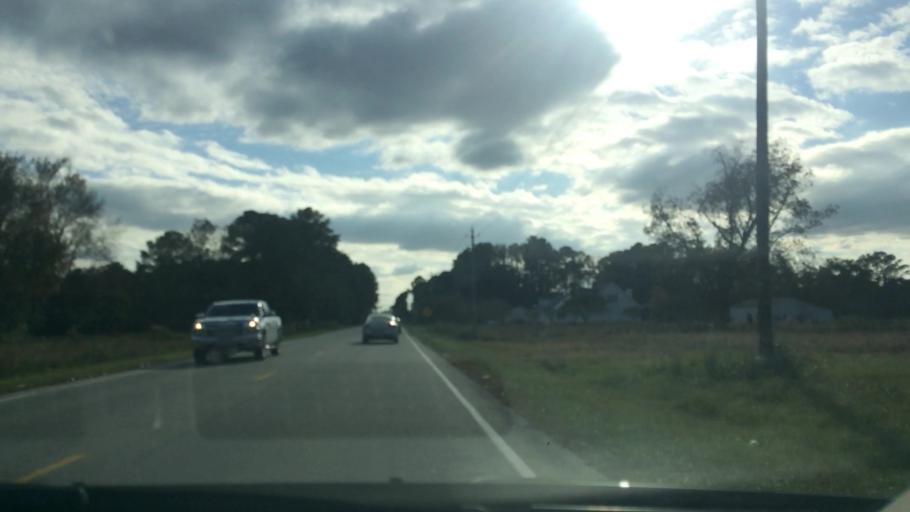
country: US
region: North Carolina
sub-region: Wayne County
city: Elroy
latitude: 35.4230
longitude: -77.8906
